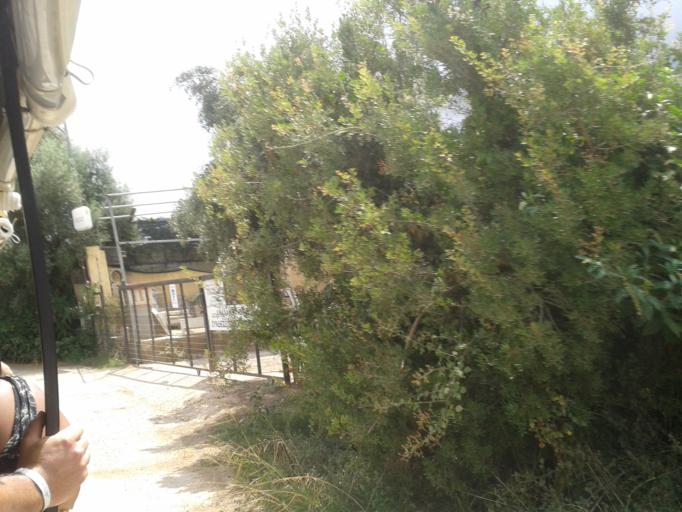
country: GR
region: Crete
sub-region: Nomos Chanias
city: Perivolia
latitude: 35.4864
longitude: 23.9802
